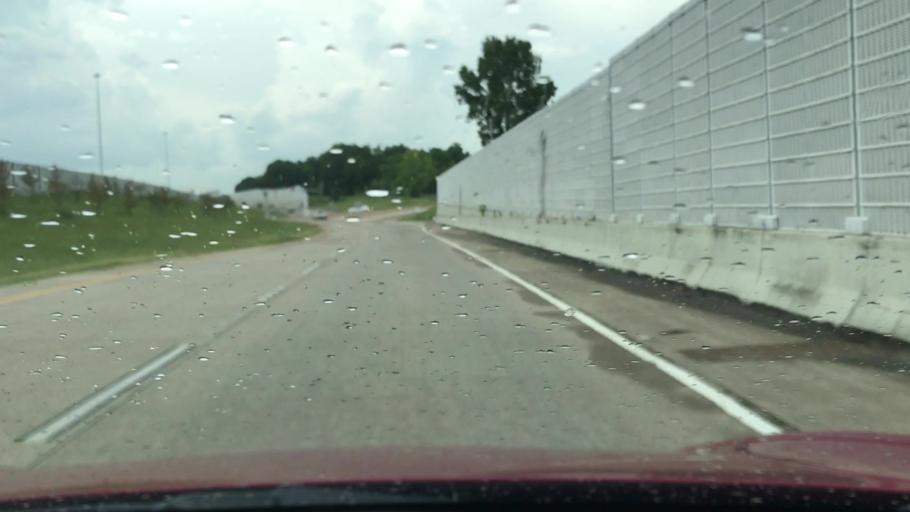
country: US
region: Louisiana
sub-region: Bossier Parish
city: Bossier City
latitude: 32.4402
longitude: -93.7559
